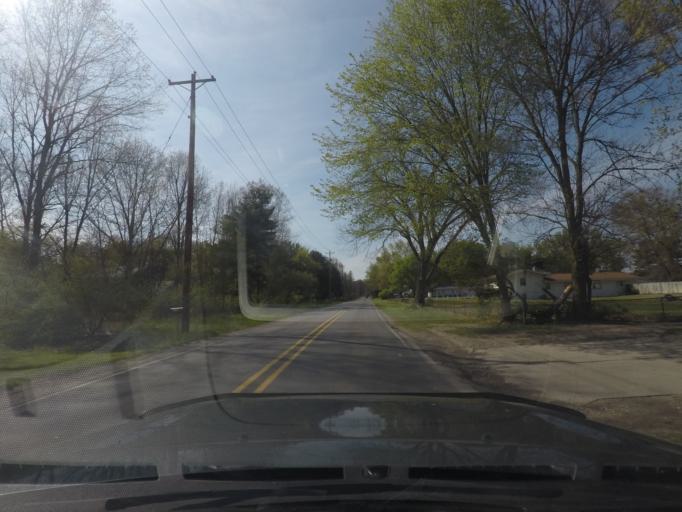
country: US
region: Indiana
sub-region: Elkhart County
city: Elkhart
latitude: 41.7082
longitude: -86.0210
